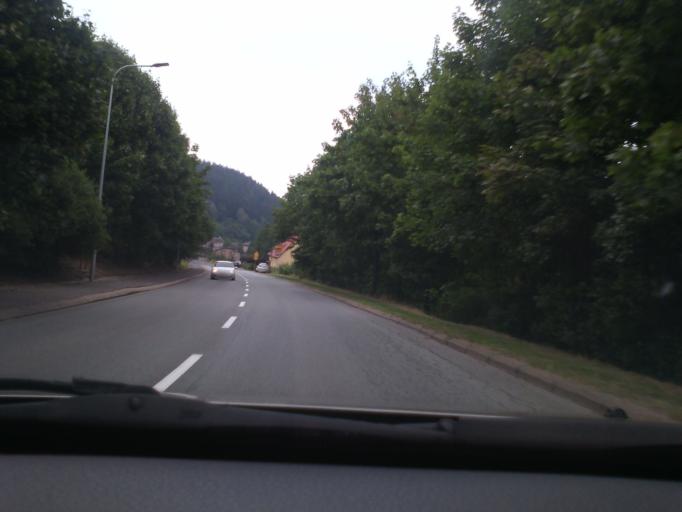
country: PL
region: Lower Silesian Voivodeship
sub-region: Powiat walbrzyski
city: Walbrzych
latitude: 50.7299
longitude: 16.2738
